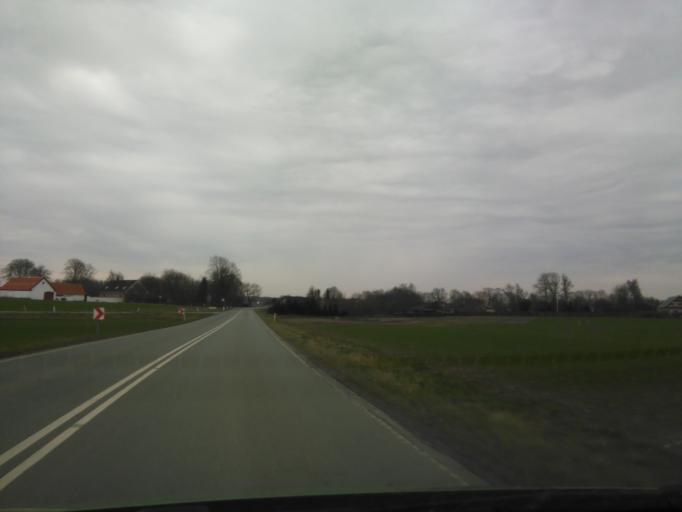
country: DK
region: Central Jutland
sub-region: Randers Kommune
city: Spentrup
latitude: 56.5393
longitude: 10.0037
